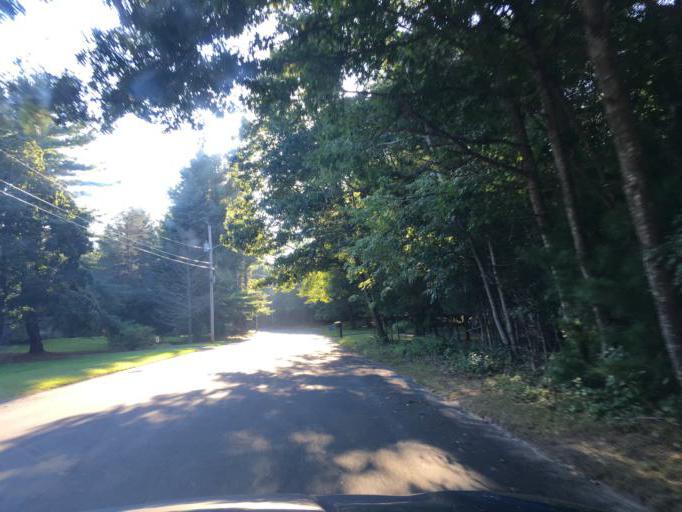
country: US
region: Rhode Island
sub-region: Kent County
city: West Warwick
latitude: 41.6451
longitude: -71.5236
